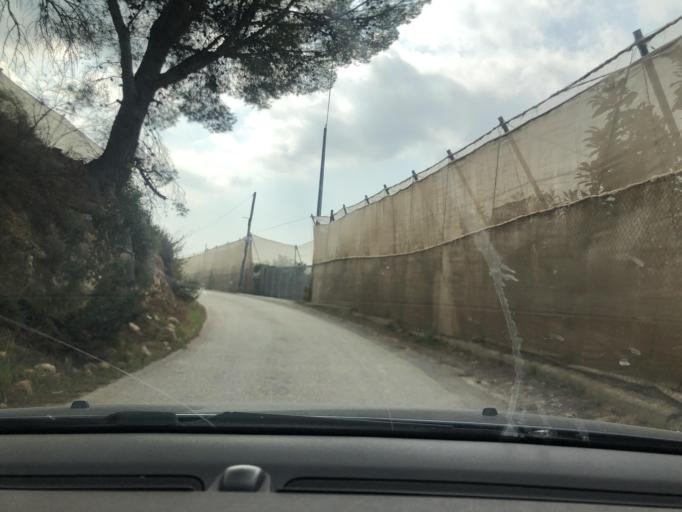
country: ES
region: Valencia
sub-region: Provincia de Alicante
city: Callosa d'En Sarria
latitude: 38.6572
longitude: -0.0946
